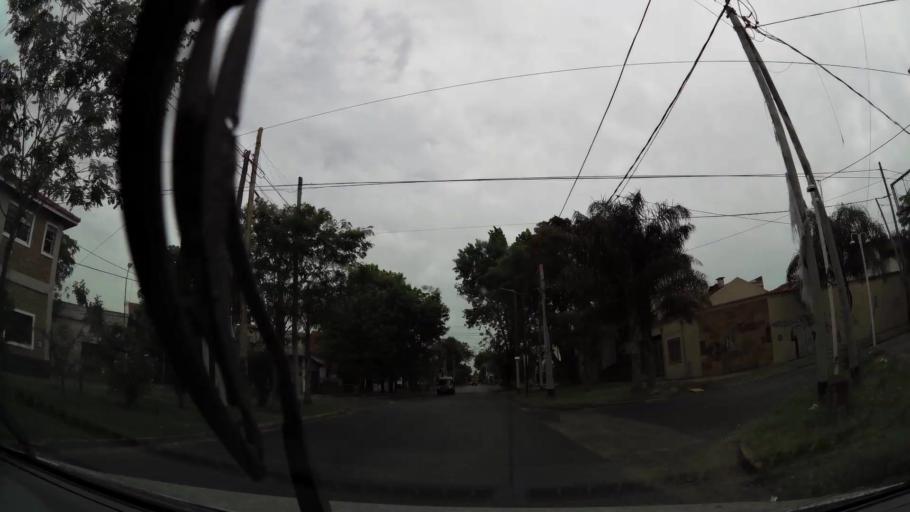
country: AR
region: Buenos Aires
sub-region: Partido de Lanus
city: Lanus
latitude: -34.6991
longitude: -58.3986
